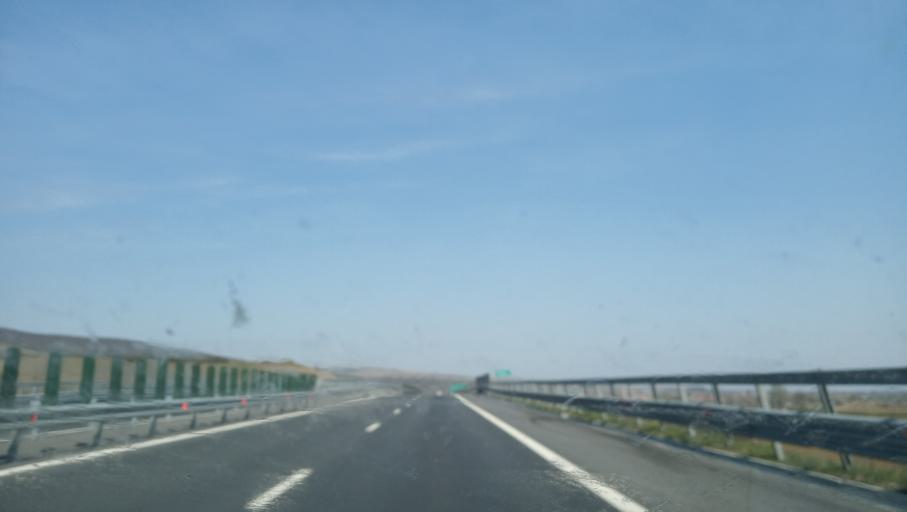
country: RO
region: Alba
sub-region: Comuna Miraslau
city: Miraslau
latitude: 46.3712
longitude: 23.7422
